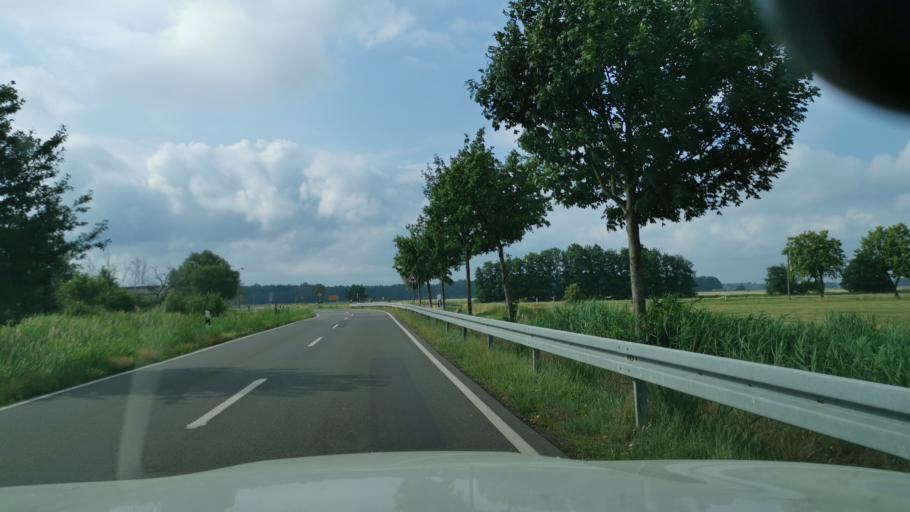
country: DE
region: Saxony-Anhalt
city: Annaburg
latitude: 51.7643
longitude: 13.0310
